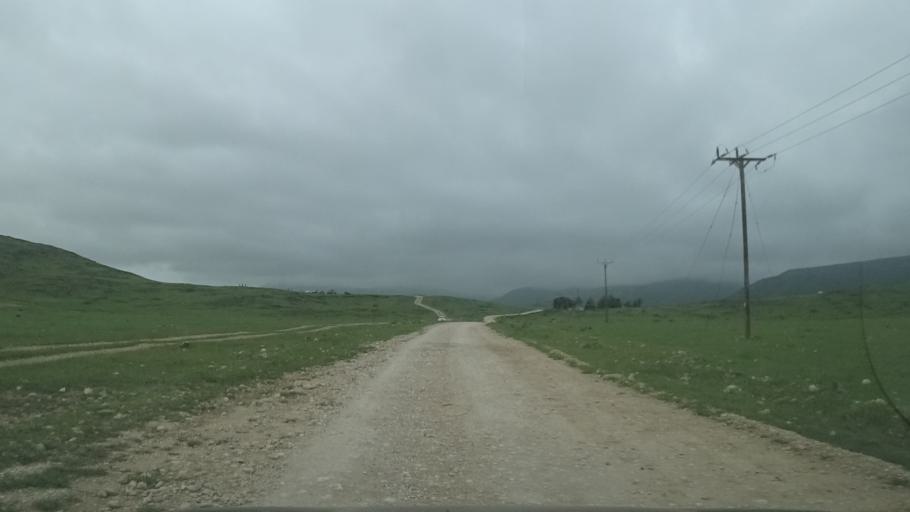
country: OM
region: Zufar
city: Salalah
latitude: 17.1155
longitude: 54.2325
